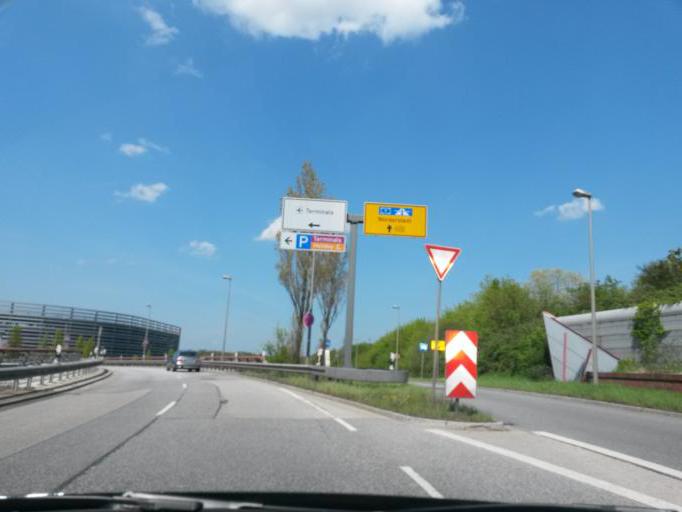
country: DE
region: Hamburg
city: Fuhlsbuettel
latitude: 53.6339
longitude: 10.0100
